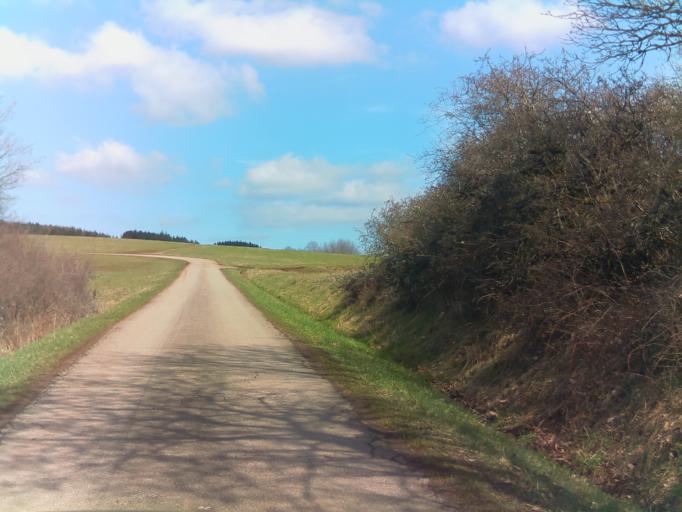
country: DE
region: Saarland
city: Nonnweiler
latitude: 49.5509
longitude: 6.9863
